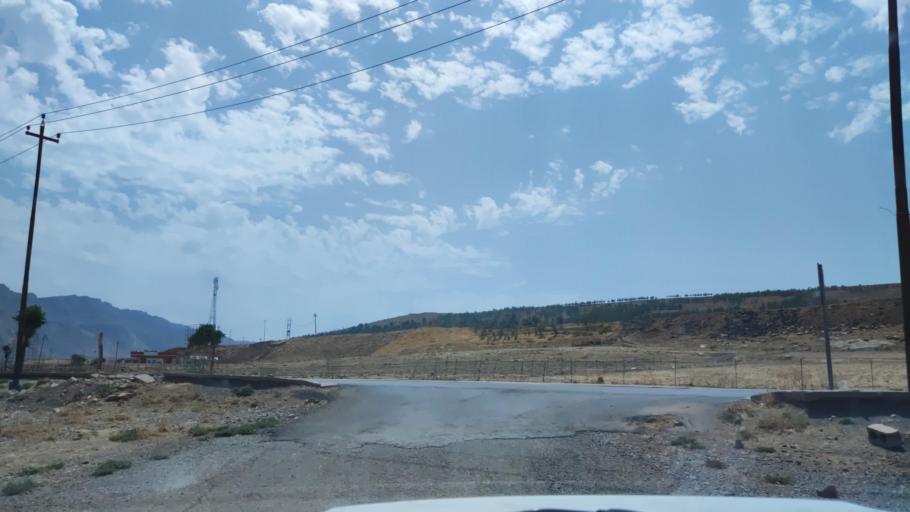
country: IQ
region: Arbil
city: Shaqlawah
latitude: 36.4969
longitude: 44.3616
